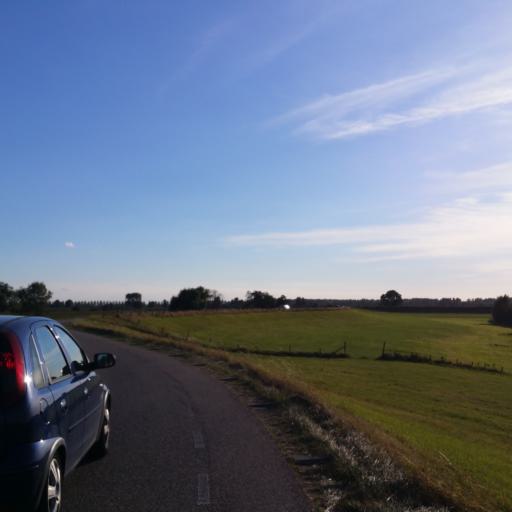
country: NL
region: Utrecht
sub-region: Gemeente IJsselstein
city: IJsselstein
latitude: 51.9765
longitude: 5.0303
